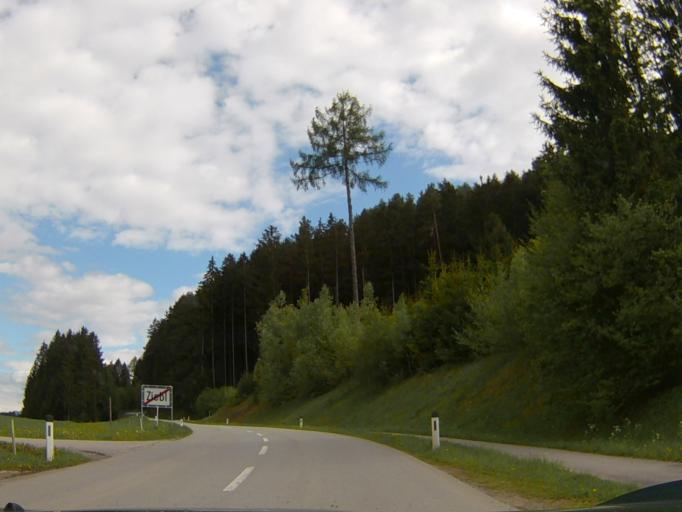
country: AT
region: Carinthia
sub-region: Politischer Bezirk Villach Land
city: Ferndorf
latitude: 46.7374
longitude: 13.5798
